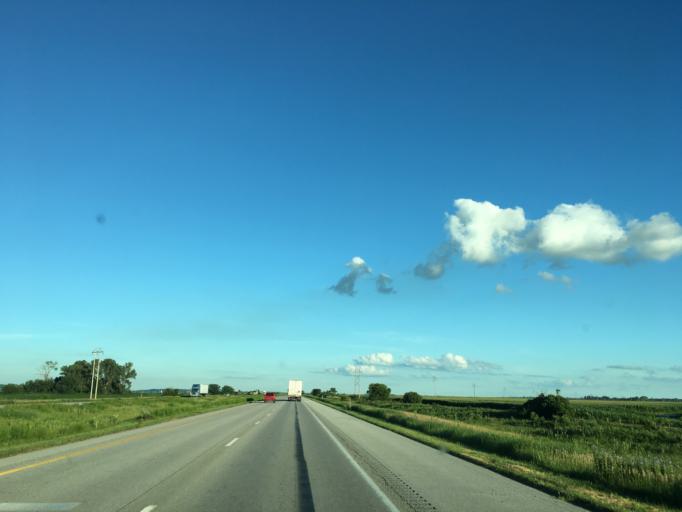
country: US
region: Nebraska
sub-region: Otoe County
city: Nebraska City
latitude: 40.6607
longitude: -95.7579
